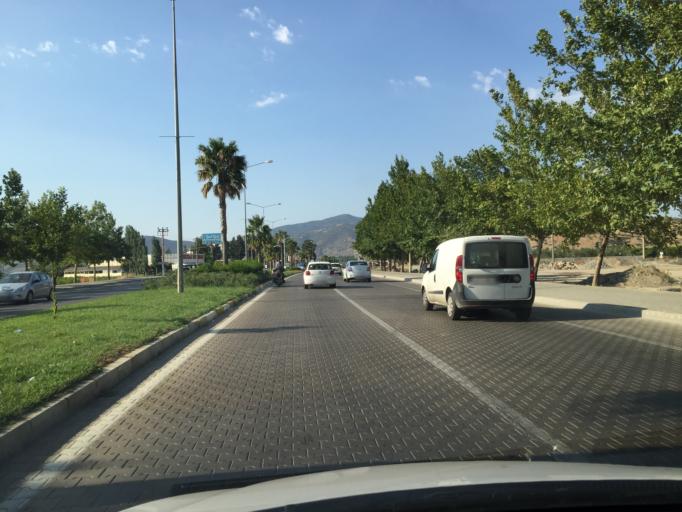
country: TR
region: Izmir
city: Selcuk
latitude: 37.9591
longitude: 27.3722
